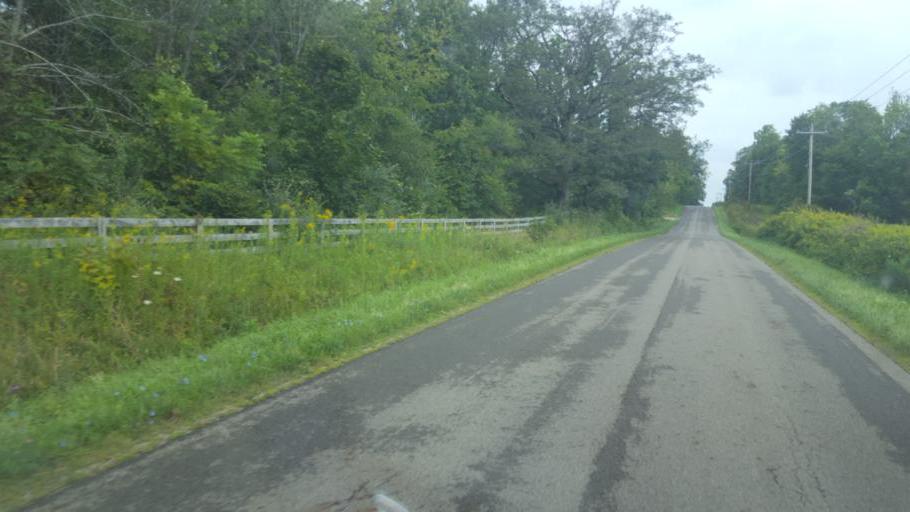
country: US
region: Ohio
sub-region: Morrow County
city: Mount Gilead
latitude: 40.5631
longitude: -82.7331
